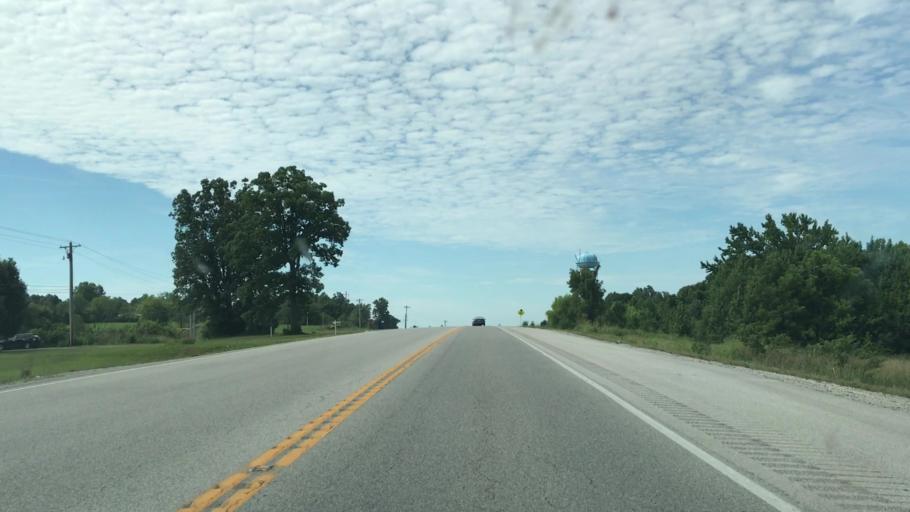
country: US
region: Kentucky
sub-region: Edmonson County
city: Brownsville
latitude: 37.1062
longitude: -86.2295
